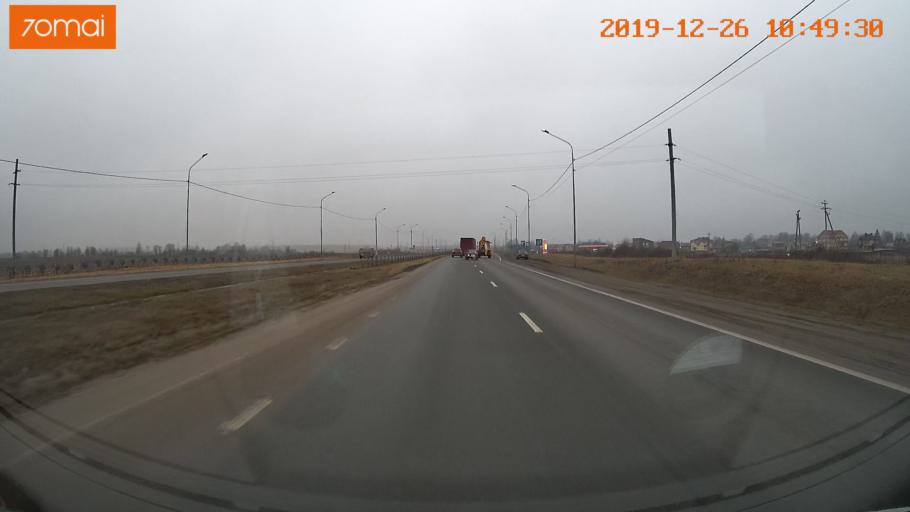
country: RU
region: Vologda
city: Molochnoye
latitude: 59.2111
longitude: 39.7128
